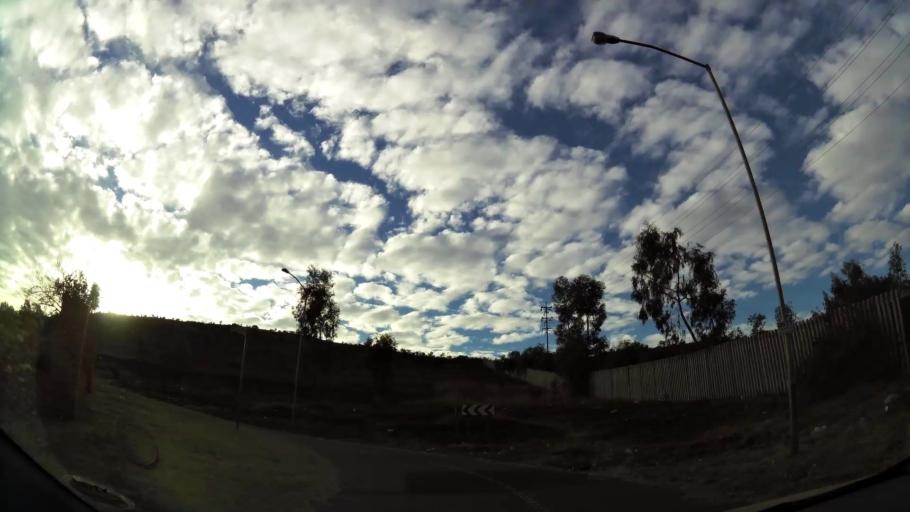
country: ZA
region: Gauteng
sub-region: City of Tshwane Metropolitan Municipality
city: Pretoria
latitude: -25.6989
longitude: 28.3225
